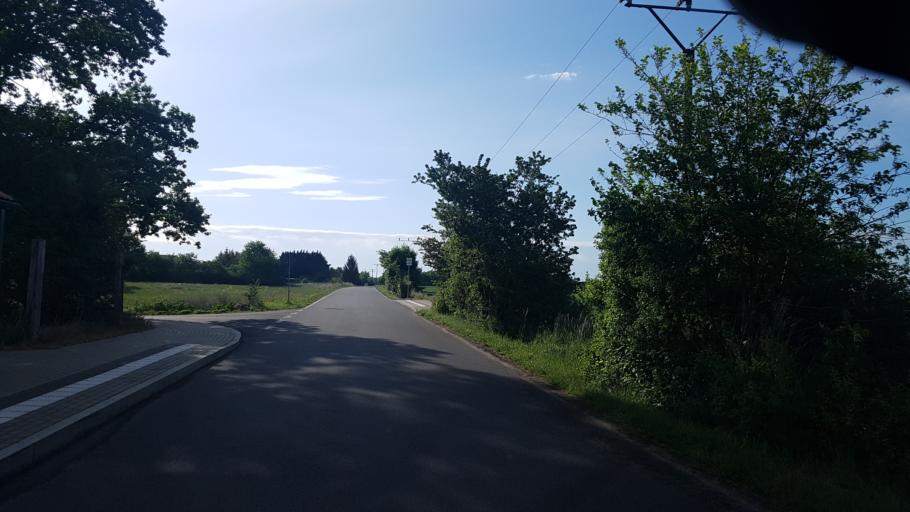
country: DE
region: Brandenburg
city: Luckau
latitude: 51.8260
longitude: 13.7559
